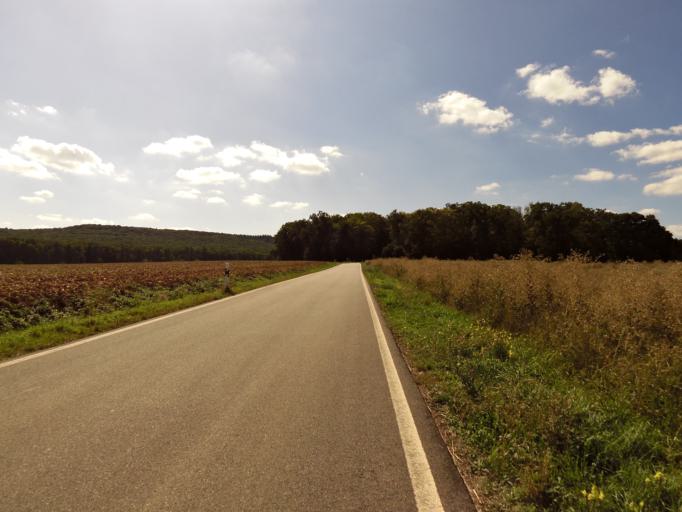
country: DE
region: Rheinland-Pfalz
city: Dreisen
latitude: 49.5860
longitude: 8.0167
